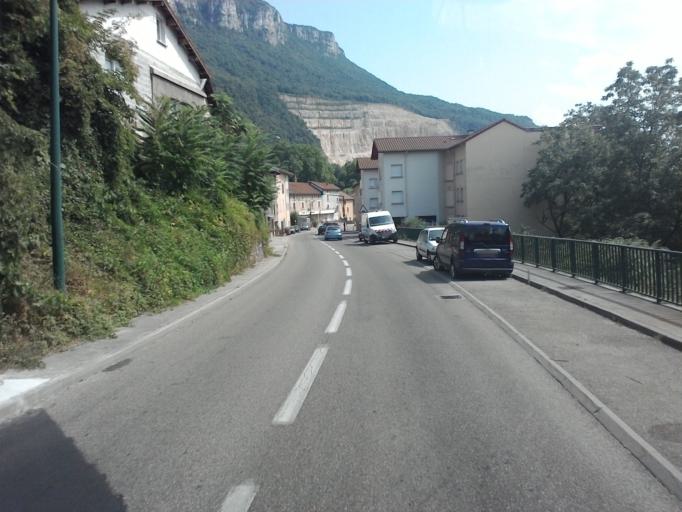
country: FR
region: Rhone-Alpes
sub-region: Departement de l'Isere
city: La Buisse
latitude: 45.3365
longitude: 5.6201
